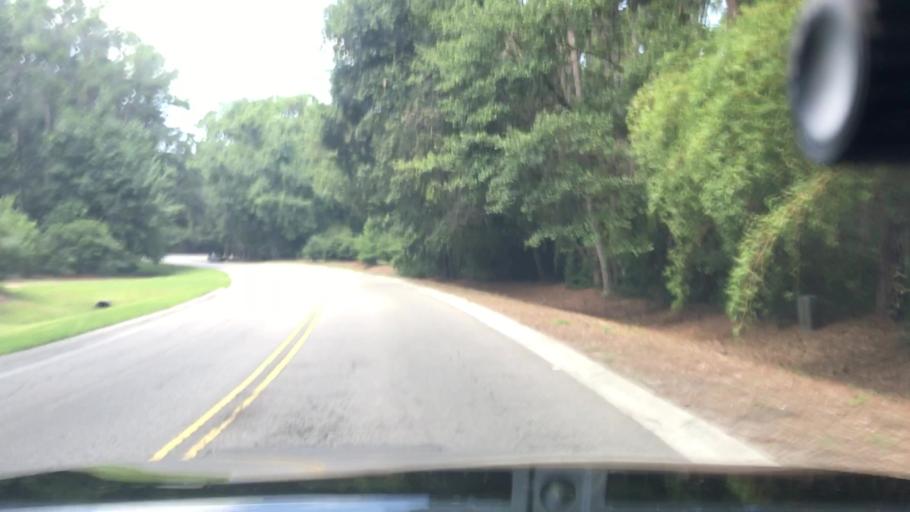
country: US
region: South Carolina
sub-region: Beaufort County
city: Hilton Head Island
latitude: 32.1490
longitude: -80.7794
